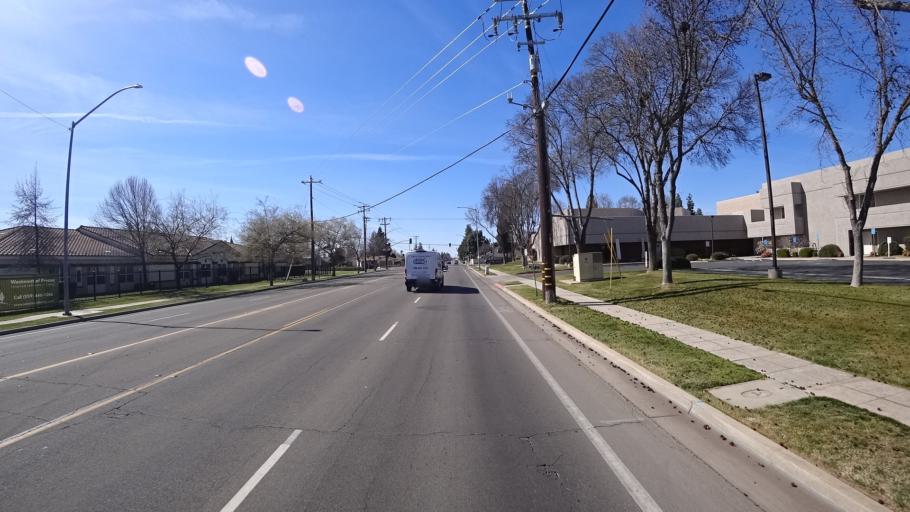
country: US
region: California
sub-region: Fresno County
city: Clovis
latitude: 36.8448
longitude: -119.7646
